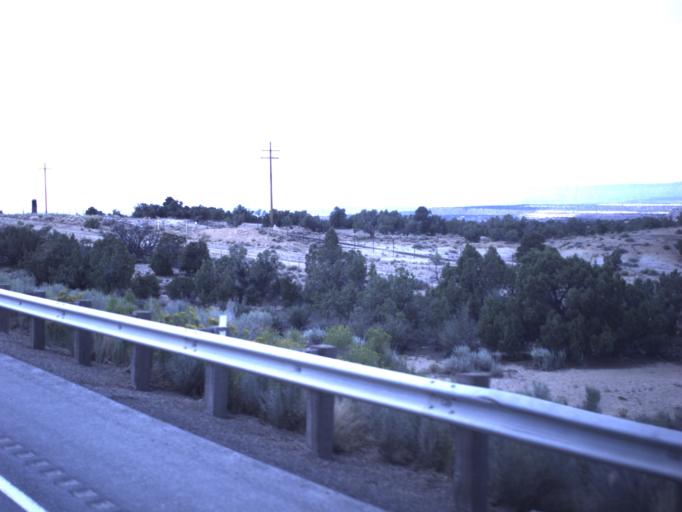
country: US
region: Utah
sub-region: Duchesne County
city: Duchesne
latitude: 40.1642
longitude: -110.4565
